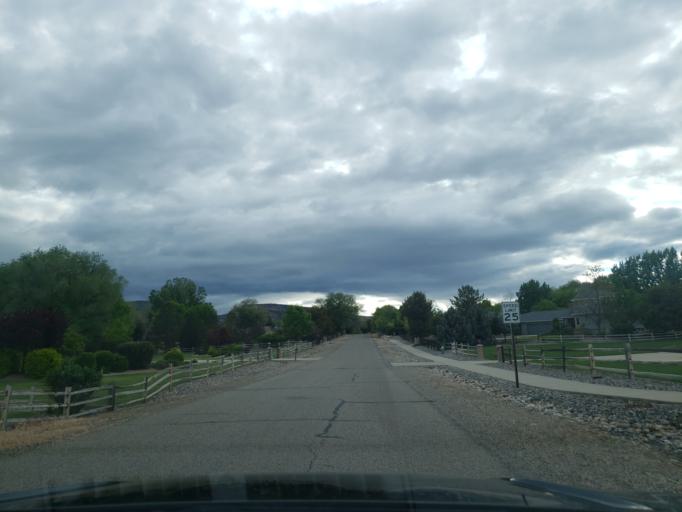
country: US
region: Colorado
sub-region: Mesa County
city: Redlands
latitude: 39.1064
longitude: -108.6754
